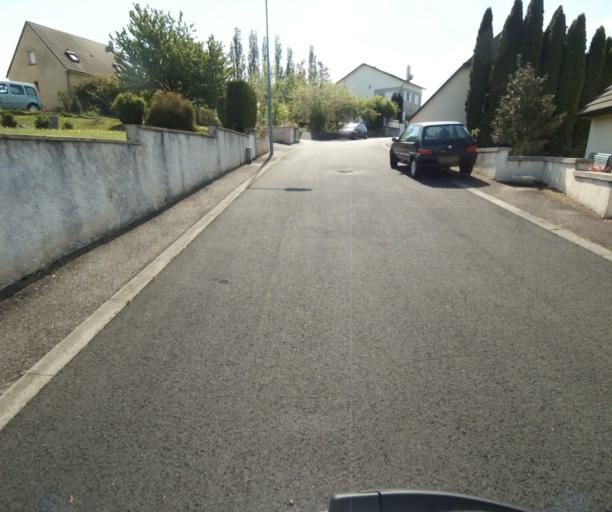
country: FR
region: Limousin
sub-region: Departement de la Correze
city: Tulle
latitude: 45.2654
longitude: 1.7773
